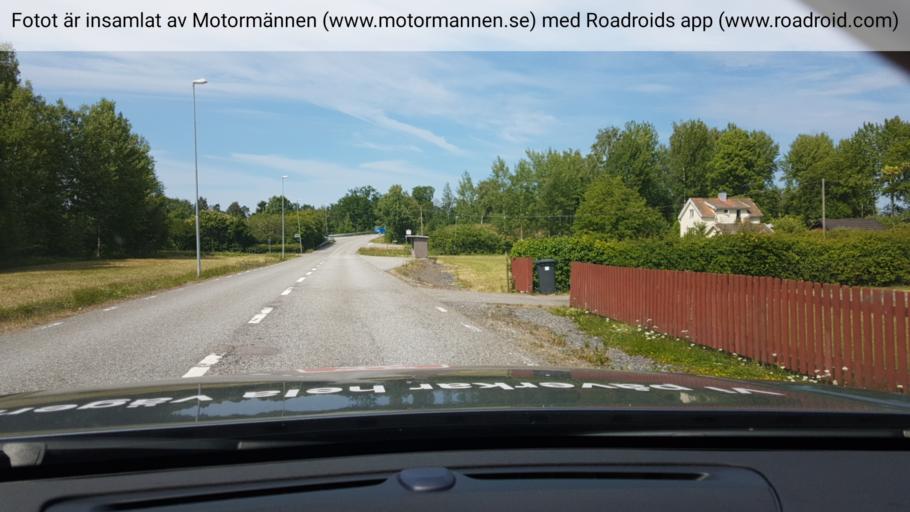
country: SE
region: Uppsala
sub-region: Osthammars Kommun
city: Marieberg
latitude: 60.1674
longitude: 18.4722
